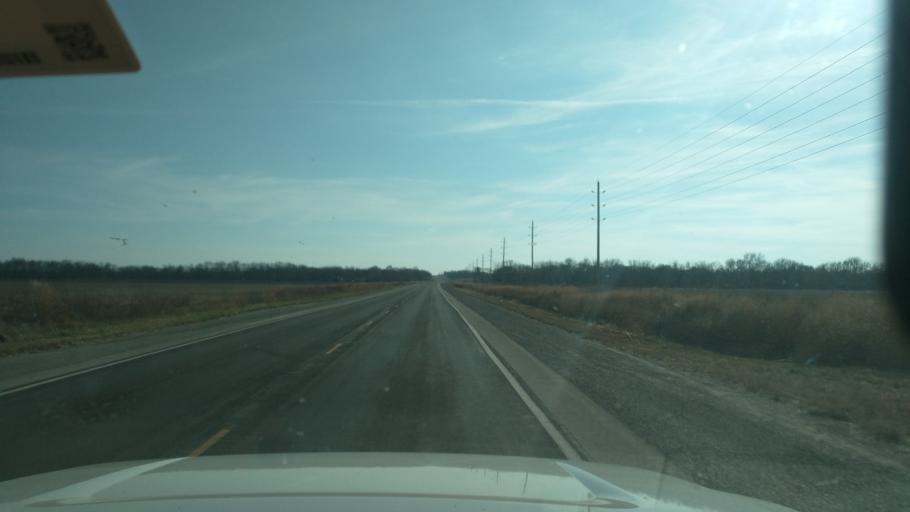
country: US
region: Kansas
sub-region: Lyon County
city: Emporia
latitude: 38.3685
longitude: -96.1802
